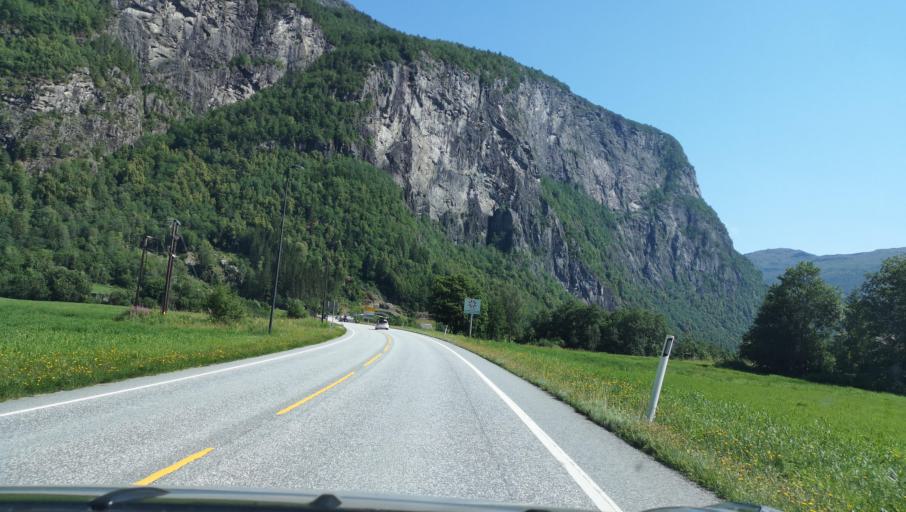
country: NO
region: Hordaland
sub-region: Granvin
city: Granvin
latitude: 60.5708
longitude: 6.6863
